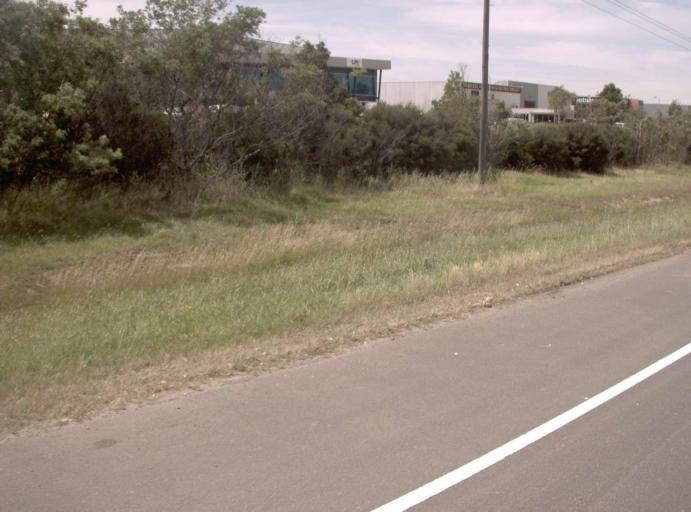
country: AU
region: Victoria
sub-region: Casey
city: Hampton Park
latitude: -38.0412
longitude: 145.2466
